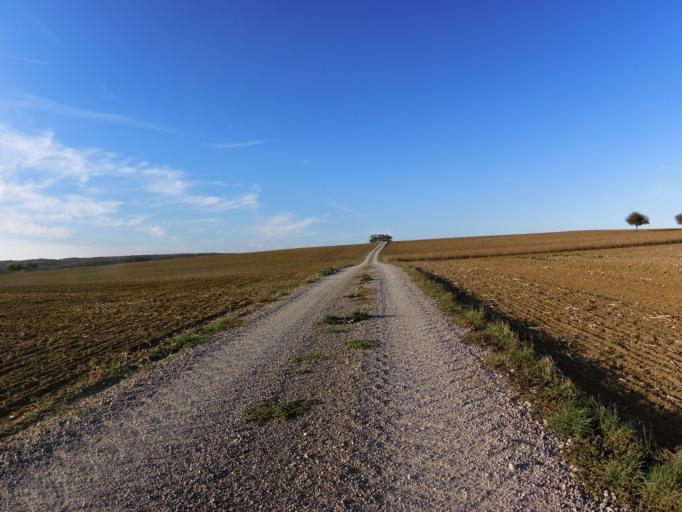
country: DE
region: Bavaria
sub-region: Regierungsbezirk Unterfranken
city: Reichenberg
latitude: 49.7260
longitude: 9.9244
